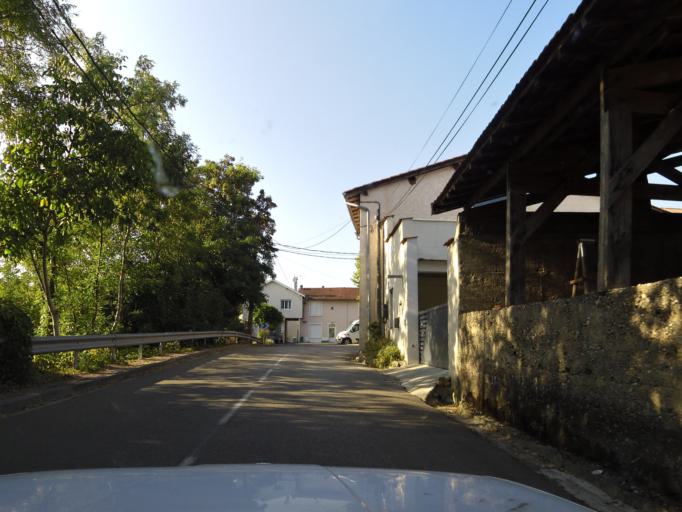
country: FR
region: Rhone-Alpes
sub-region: Departement de l'Ain
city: Chazey-sur-Ain
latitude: 45.8917
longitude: 5.2530
